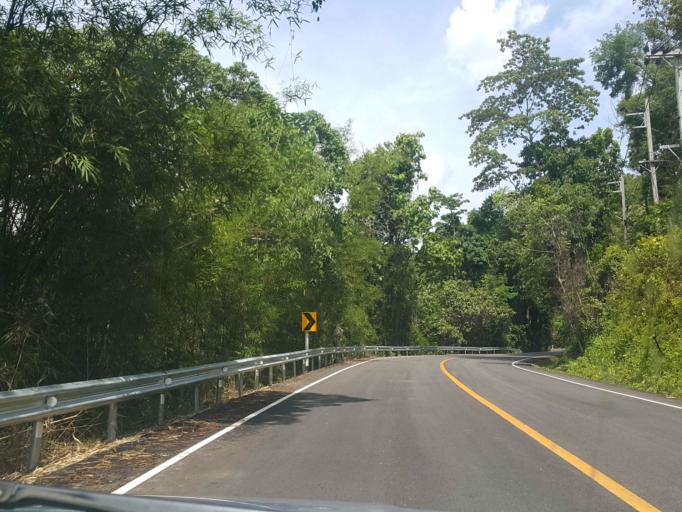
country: TH
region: Nan
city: Ban Luang
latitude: 18.8737
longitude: 100.5166
